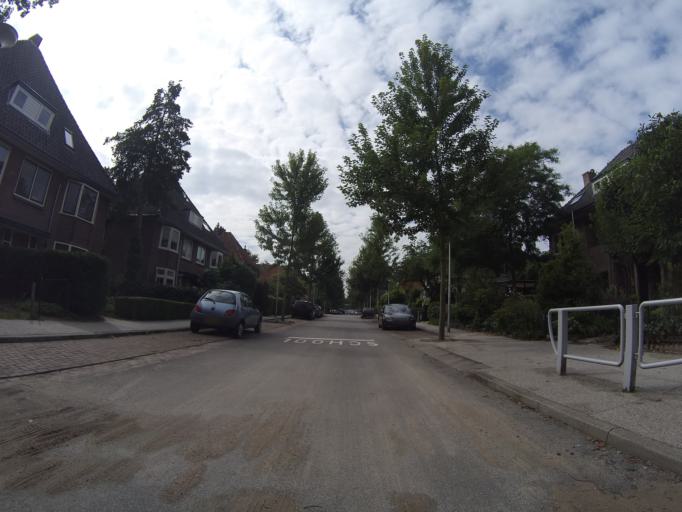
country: NL
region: Utrecht
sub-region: Gemeente Amersfoort
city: Amersfoort
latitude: 52.1429
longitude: 5.3738
